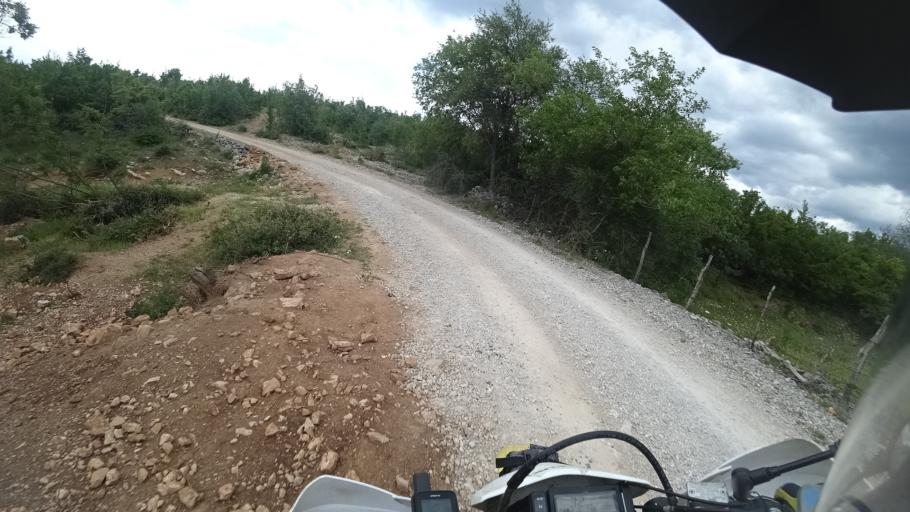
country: HR
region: Sibensko-Kniniska
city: Kistanje
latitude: 44.0964
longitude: 16.0090
